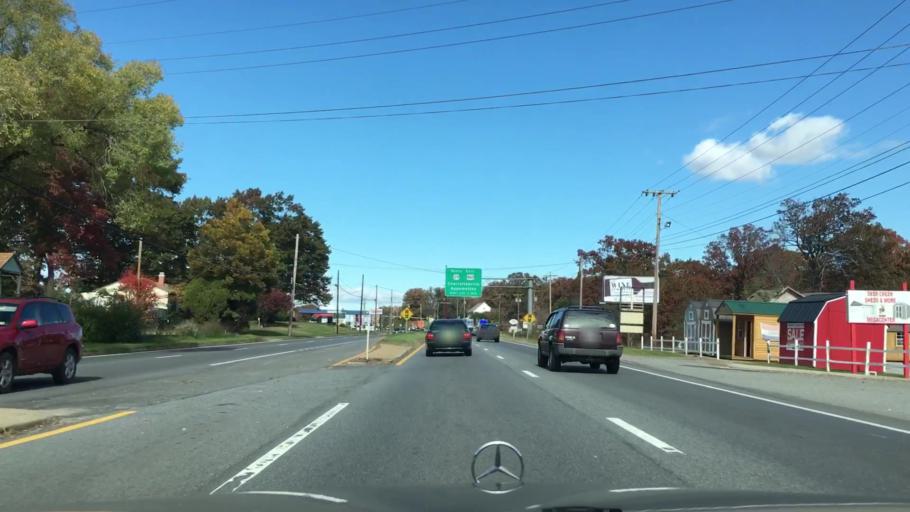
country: US
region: Virginia
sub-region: Campbell County
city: Timberlake
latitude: 37.3222
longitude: -79.1896
